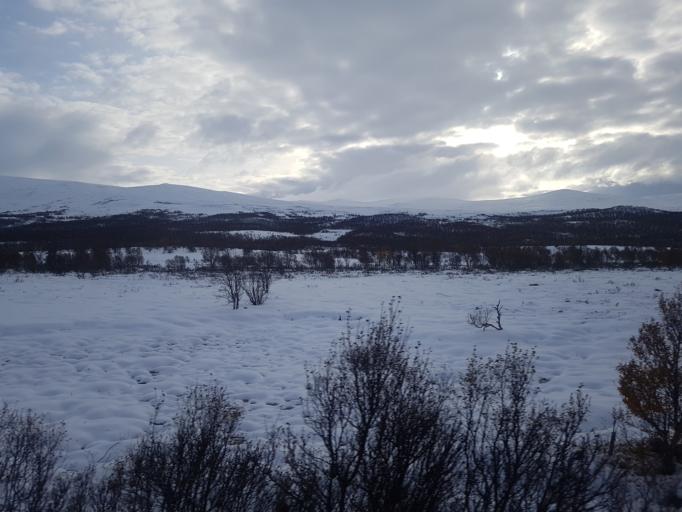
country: NO
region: Oppland
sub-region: Dovre
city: Dovre
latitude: 62.1164
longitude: 9.2843
